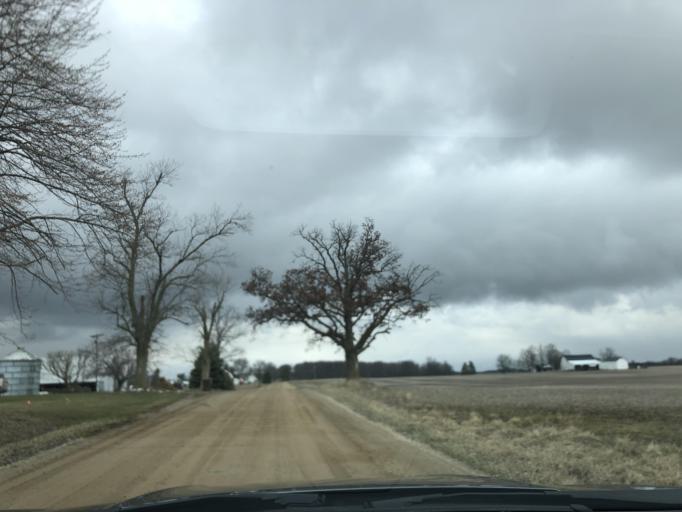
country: US
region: Michigan
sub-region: Clinton County
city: Saint Johns
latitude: 43.0924
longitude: -84.6106
